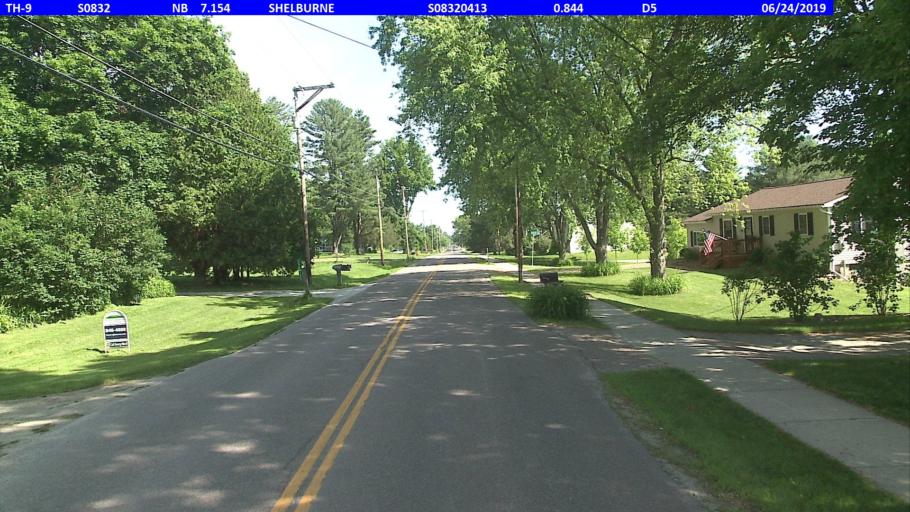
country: US
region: Vermont
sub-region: Chittenden County
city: Burlington
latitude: 44.3672
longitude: -73.2238
